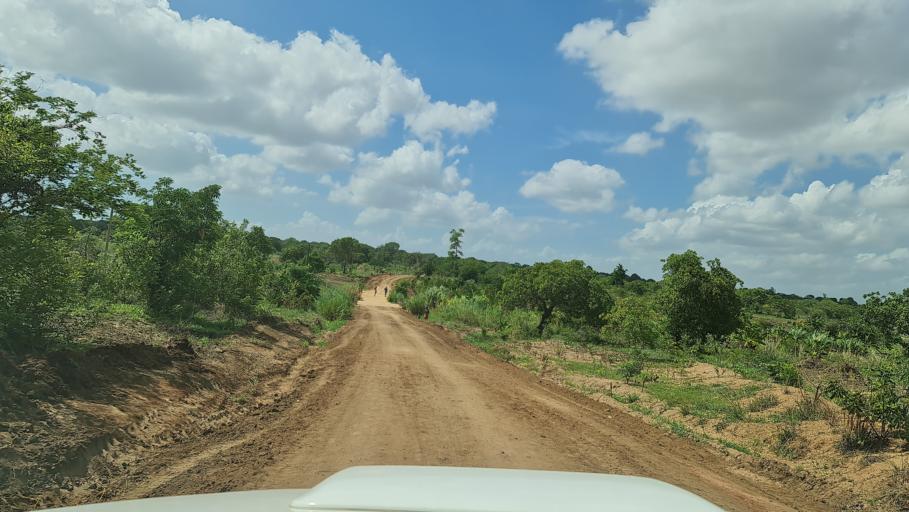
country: MZ
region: Nampula
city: Ilha de Mocambique
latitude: -15.0116
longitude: 40.5603
